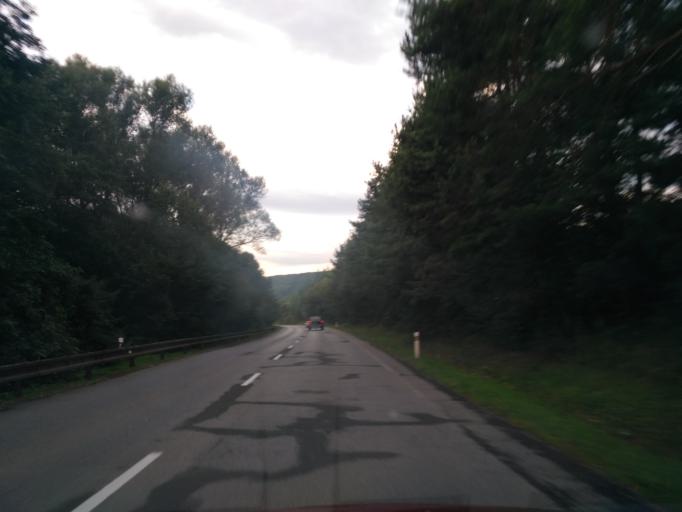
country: SK
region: Presovsky
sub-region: Okres Presov
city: Presov
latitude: 48.9614
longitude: 21.1648
